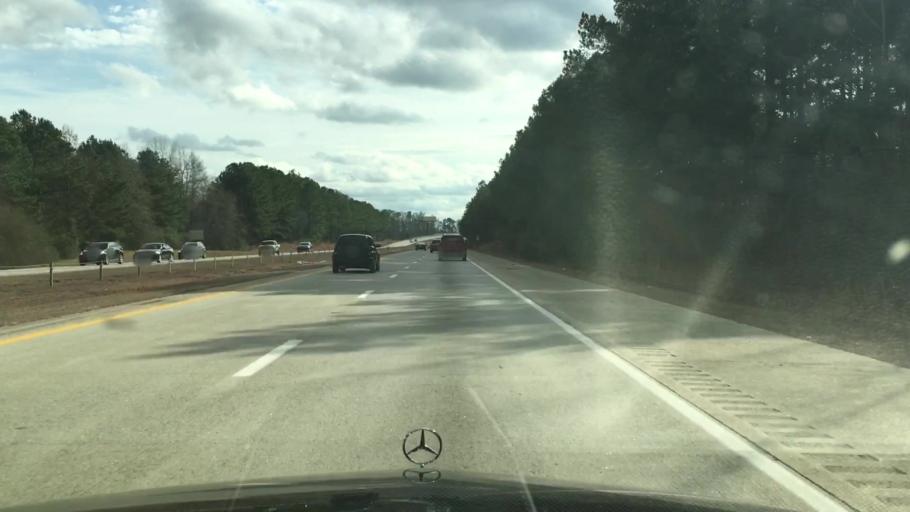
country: US
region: North Carolina
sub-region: Johnston County
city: Benson
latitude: 35.4169
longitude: -78.5274
